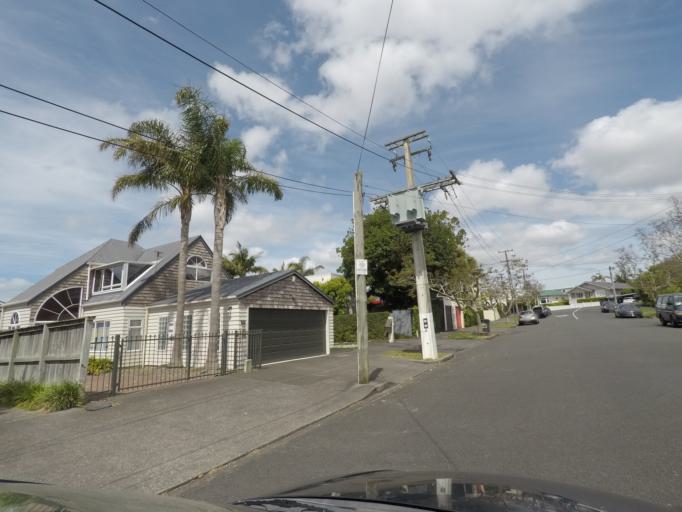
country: NZ
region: Auckland
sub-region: Auckland
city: Auckland
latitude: -36.8515
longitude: 174.7197
